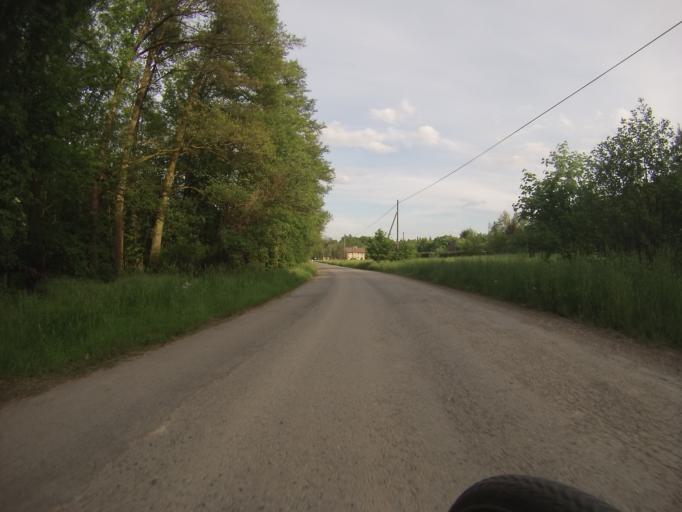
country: CZ
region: Olomoucky
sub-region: Okres Prostejov
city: Plumlov
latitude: 49.4658
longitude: 16.9761
